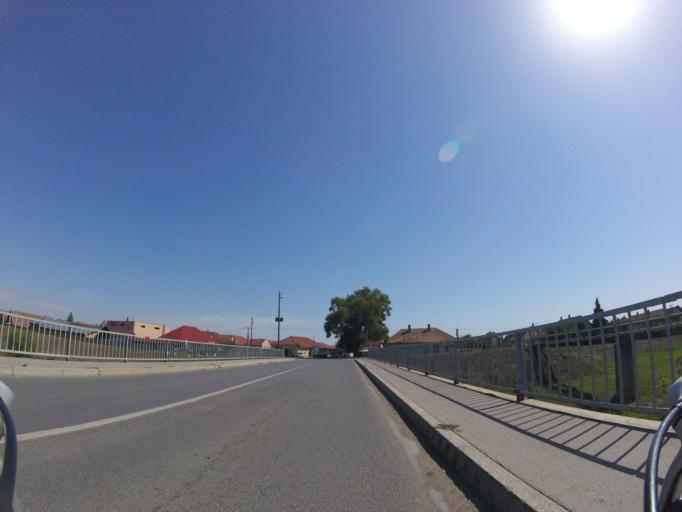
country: HU
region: Szabolcs-Szatmar-Bereg
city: Nagyecsed
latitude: 47.8624
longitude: 22.3873
